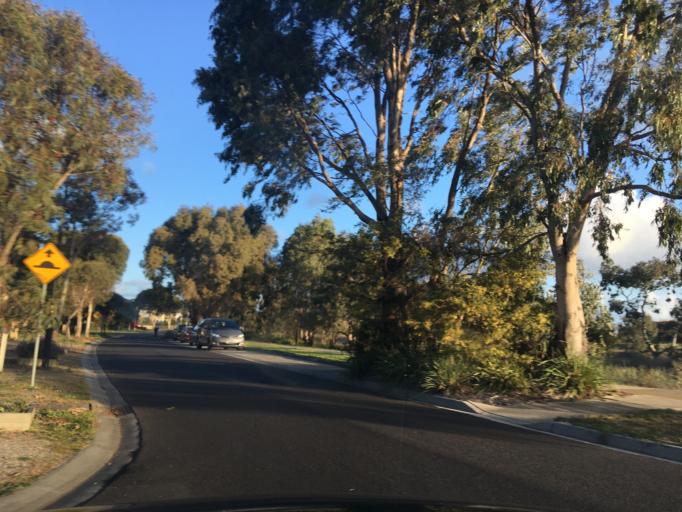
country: AU
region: Victoria
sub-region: Wyndham
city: Williams Landing
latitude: -37.8813
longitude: 144.7390
